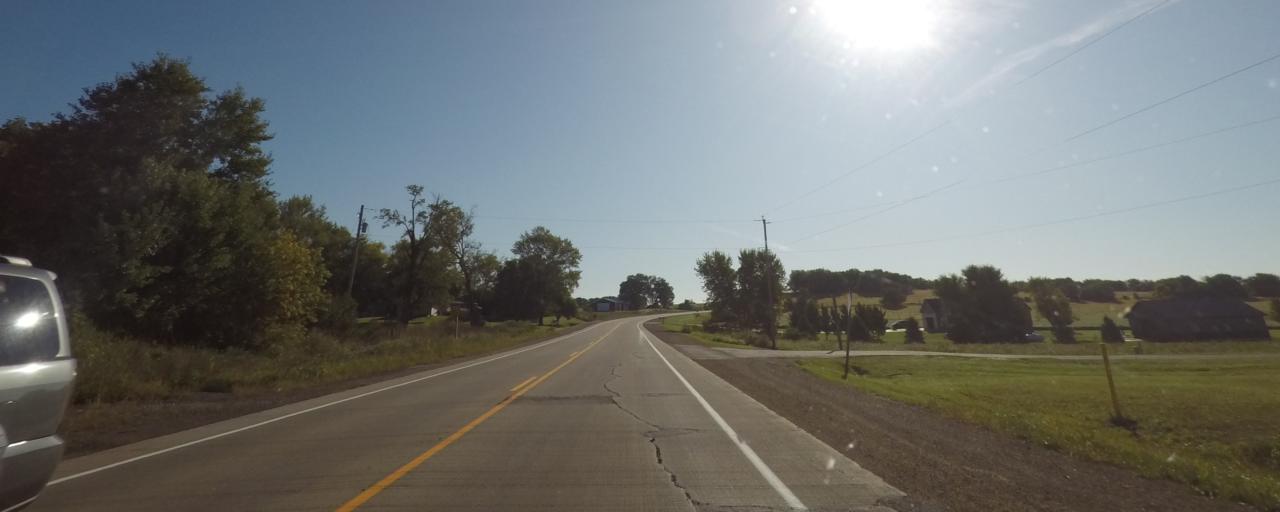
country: US
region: Wisconsin
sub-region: Dane County
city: Deerfield
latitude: 43.0368
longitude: -89.0996
